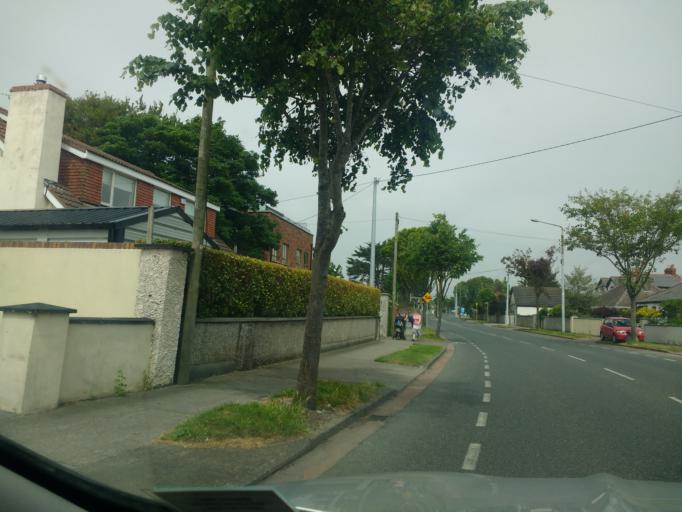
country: IE
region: Leinster
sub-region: Fingal County
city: Baldoyle
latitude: 53.3900
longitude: -6.1239
